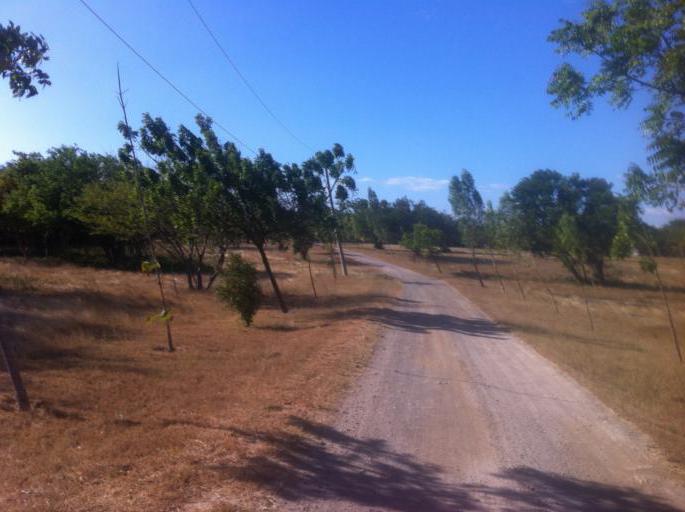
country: NI
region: Managua
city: Carlos Fonseca Amador
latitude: 11.9009
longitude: -86.6074
